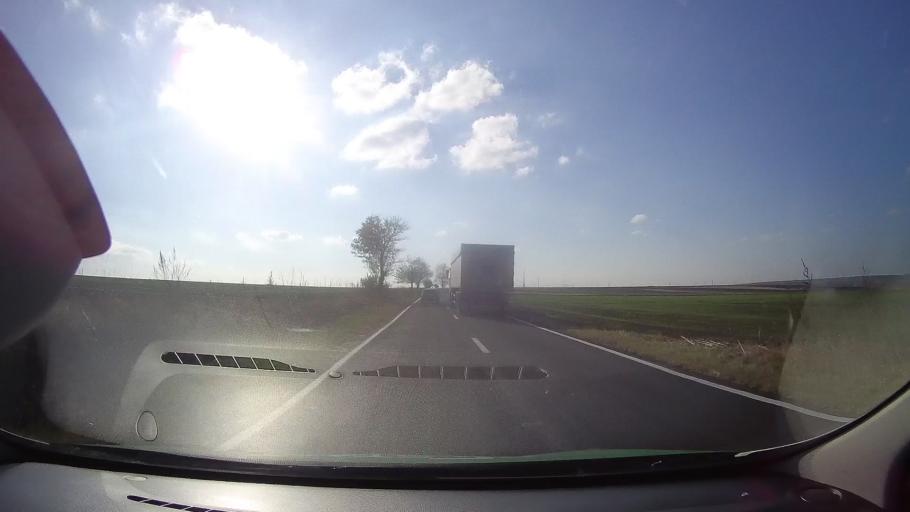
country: RO
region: Tulcea
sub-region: Comuna Topolog
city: Topolog
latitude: 44.8422
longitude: 28.3076
